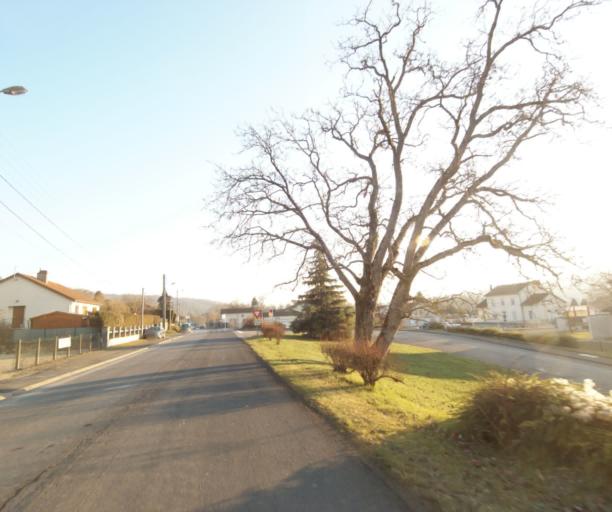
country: FR
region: Champagne-Ardenne
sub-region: Departement de la Haute-Marne
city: Chevillon
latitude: 48.5255
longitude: 5.1122
